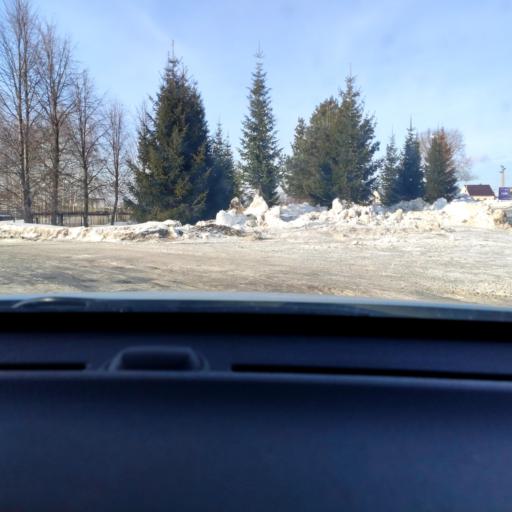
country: RU
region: Tatarstan
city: Osinovo
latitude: 55.8636
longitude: 48.8365
